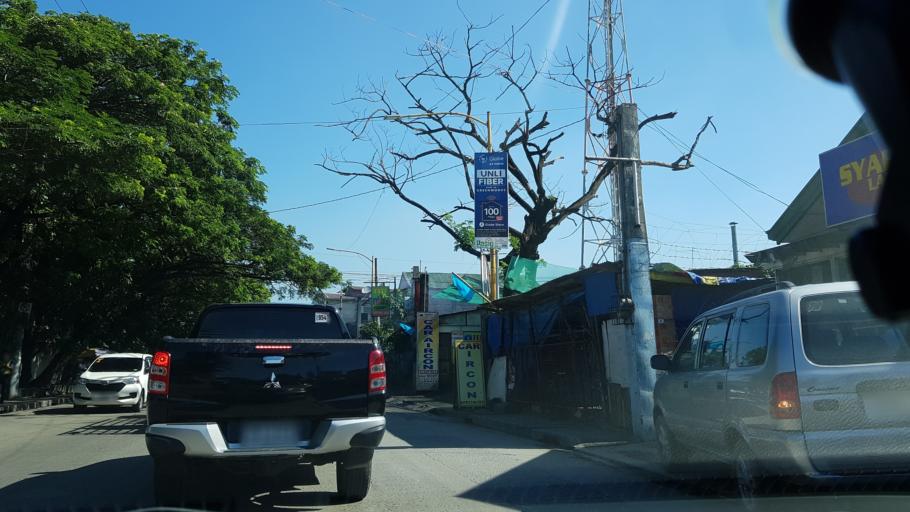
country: PH
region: Calabarzon
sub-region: Province of Rizal
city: Cainta
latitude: 14.5663
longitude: 121.0942
